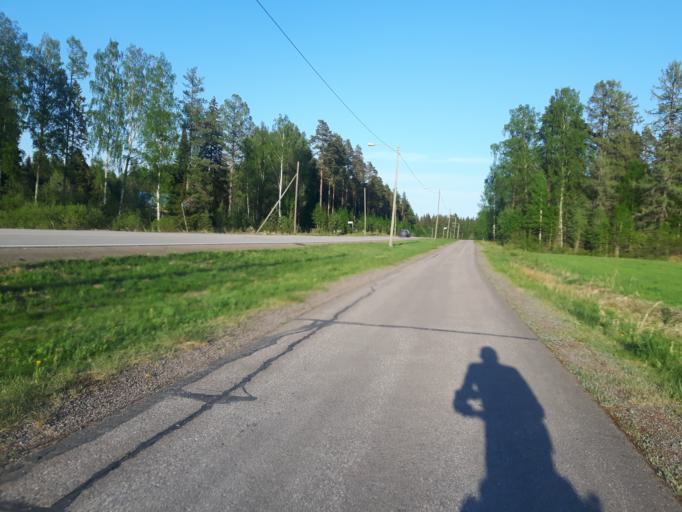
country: FI
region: Uusimaa
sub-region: Loviisa
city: Lovisa
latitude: 60.4564
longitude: 26.1434
